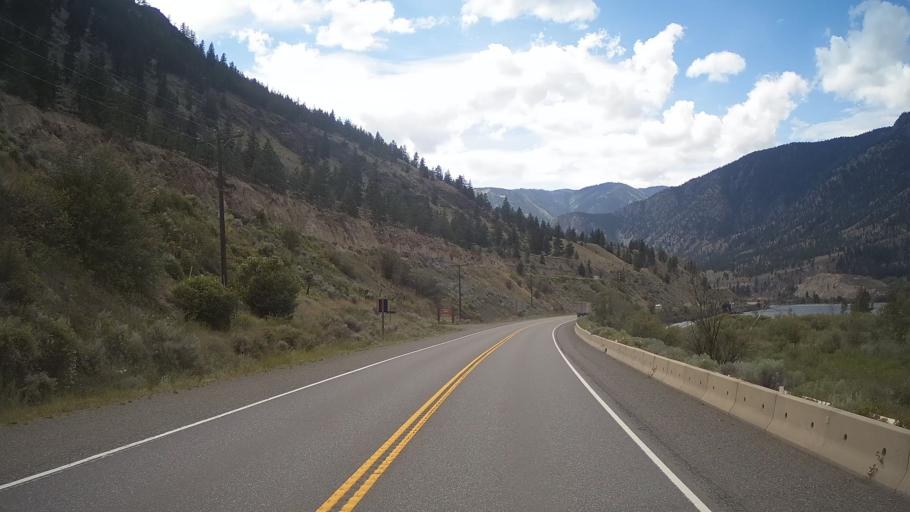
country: CA
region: British Columbia
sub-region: Thompson-Nicola Regional District
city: Ashcroft
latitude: 50.4119
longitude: -121.3615
